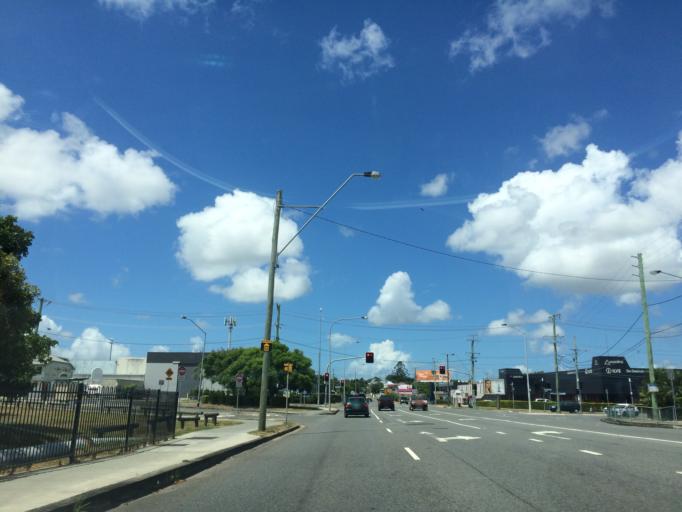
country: AU
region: Queensland
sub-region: Brisbane
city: Woolloongabba
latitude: -27.4876
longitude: 153.0534
